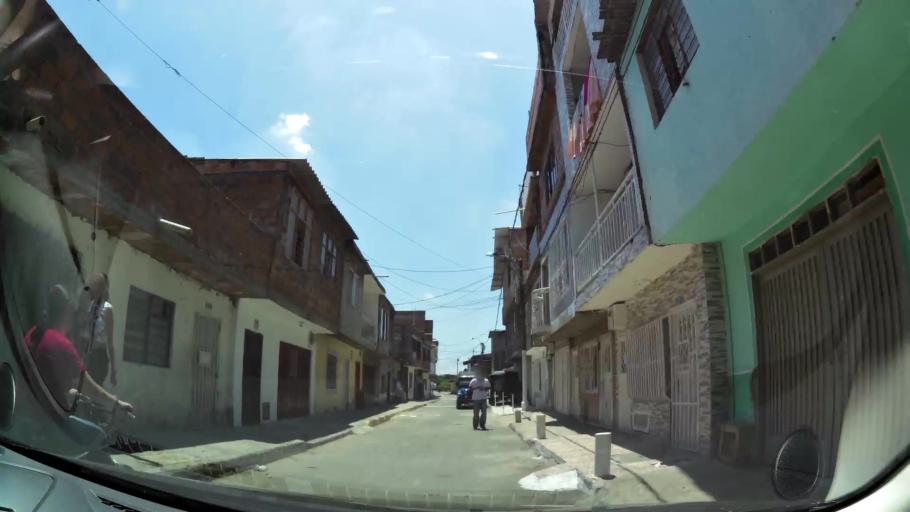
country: CO
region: Valle del Cauca
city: Cali
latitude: 3.4281
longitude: -76.5050
